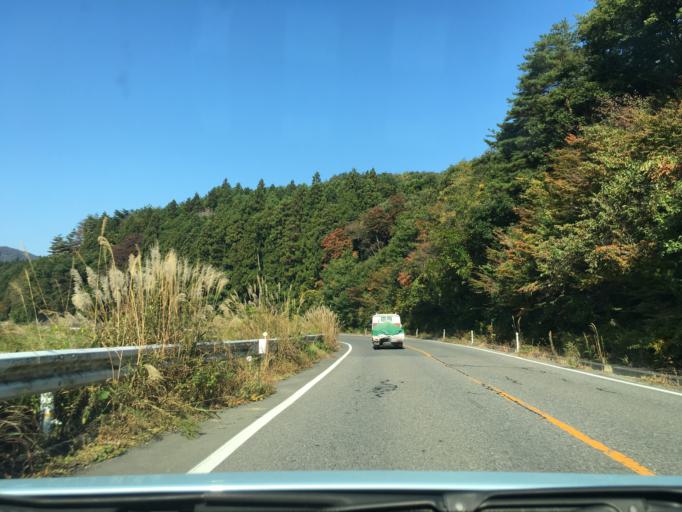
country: JP
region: Fukushima
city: Sukagawa
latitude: 37.2912
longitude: 140.1794
